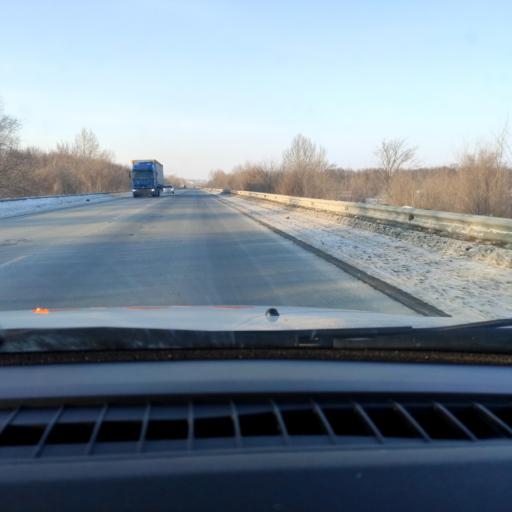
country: RU
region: Samara
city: Kinel'
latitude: 53.2016
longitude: 50.5097
